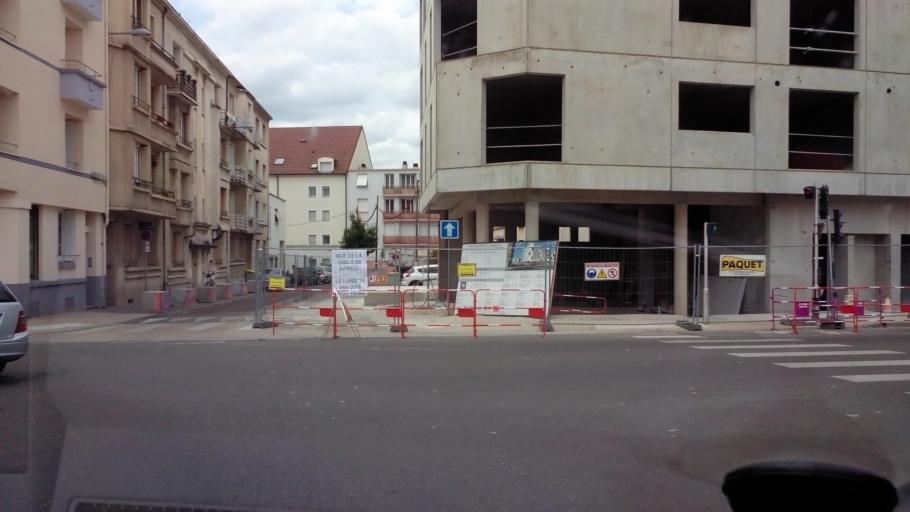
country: FR
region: Bourgogne
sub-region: Departement de la Cote-d'Or
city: Fontaine-les-Dijon
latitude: 47.3299
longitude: 5.0433
